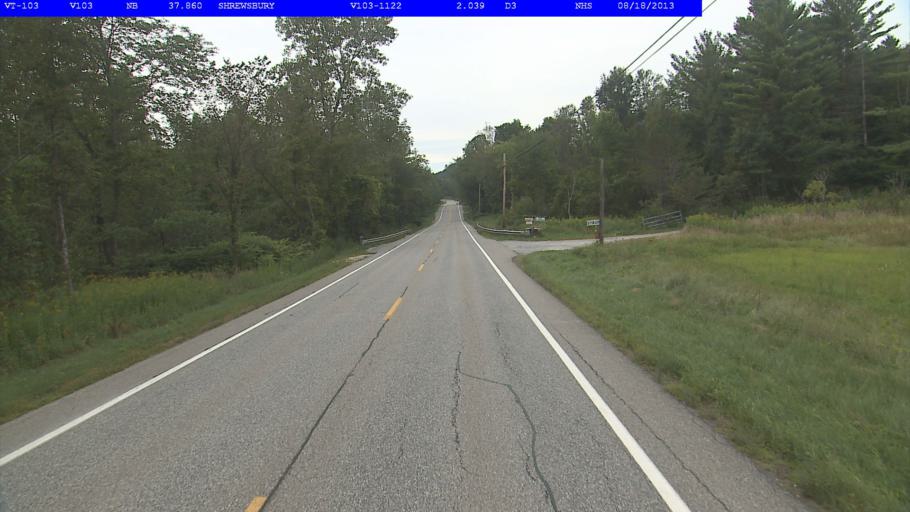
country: US
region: Vermont
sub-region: Rutland County
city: Rutland
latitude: 43.5024
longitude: -72.8998
